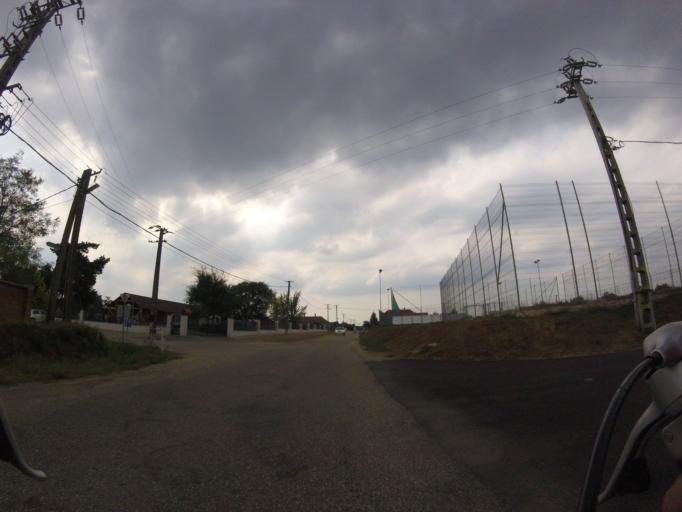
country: HU
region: Szabolcs-Szatmar-Bereg
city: Nyirpazony
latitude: 48.0141
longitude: 21.8230
